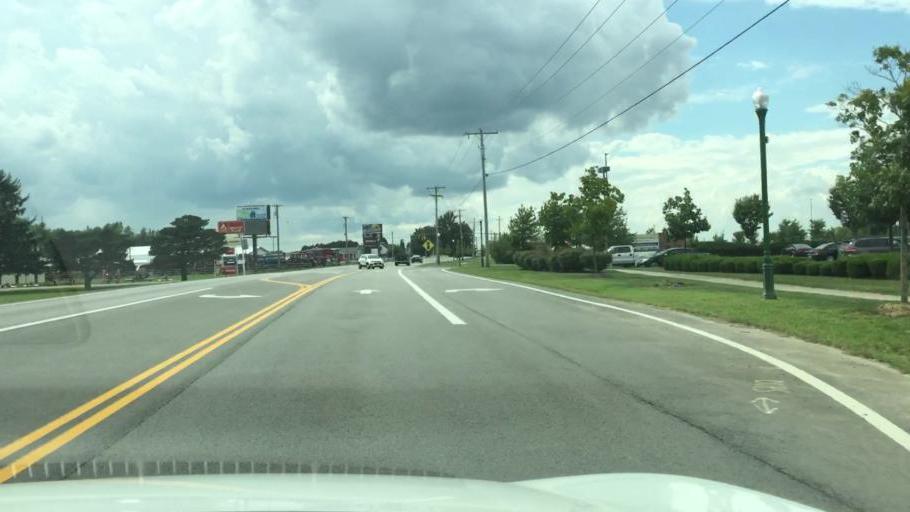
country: US
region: Ohio
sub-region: Champaign County
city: Urbana
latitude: 40.1064
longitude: -83.7145
